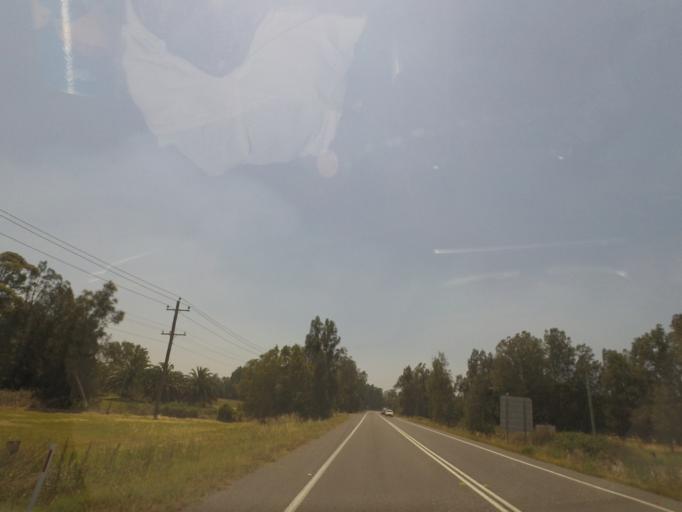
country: AU
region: New South Wales
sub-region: Port Stephens Shire
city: Medowie
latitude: -32.8046
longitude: 151.8791
